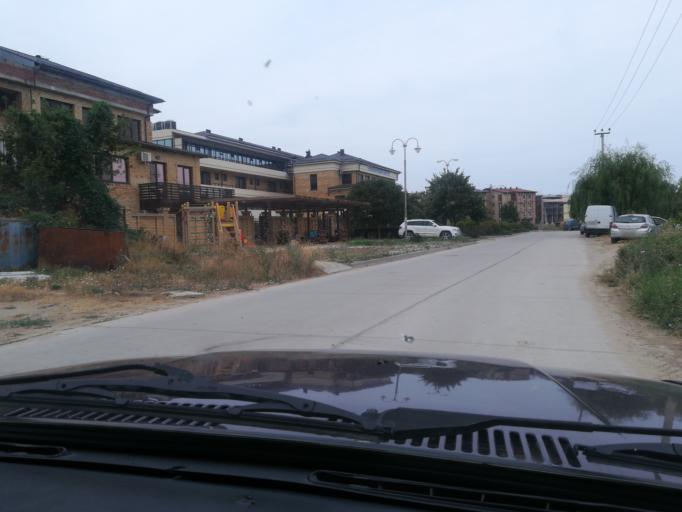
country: RU
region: Krasnodarskiy
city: Vityazevo
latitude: 44.9913
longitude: 37.2577
